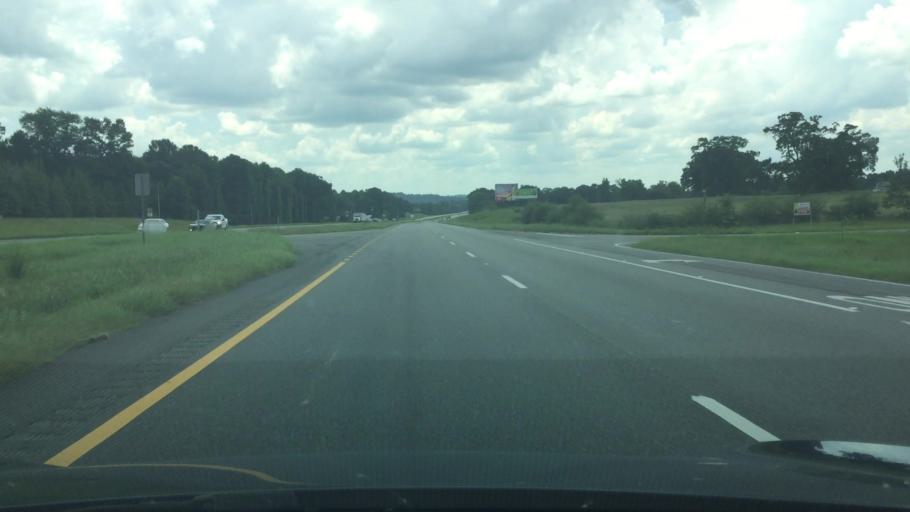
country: US
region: Alabama
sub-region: Pike County
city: Troy
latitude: 31.8760
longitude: -86.0031
